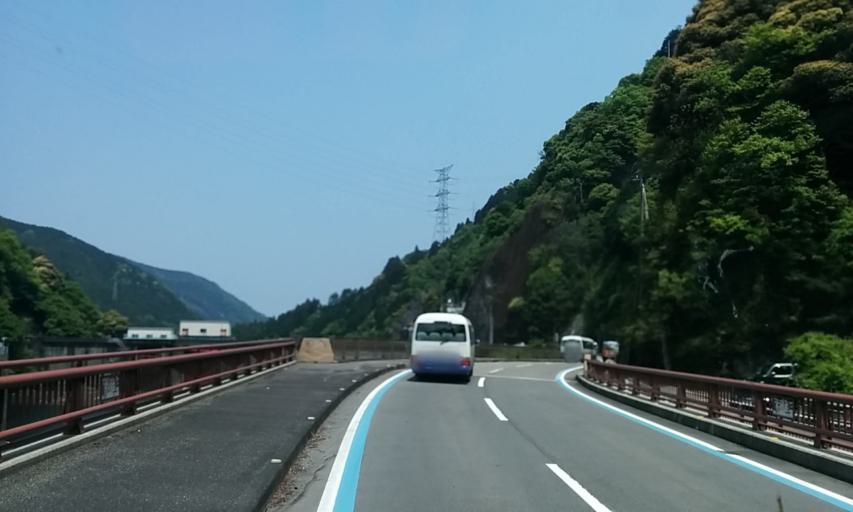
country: JP
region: Ehime
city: Niihama
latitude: 33.8918
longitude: 133.3101
